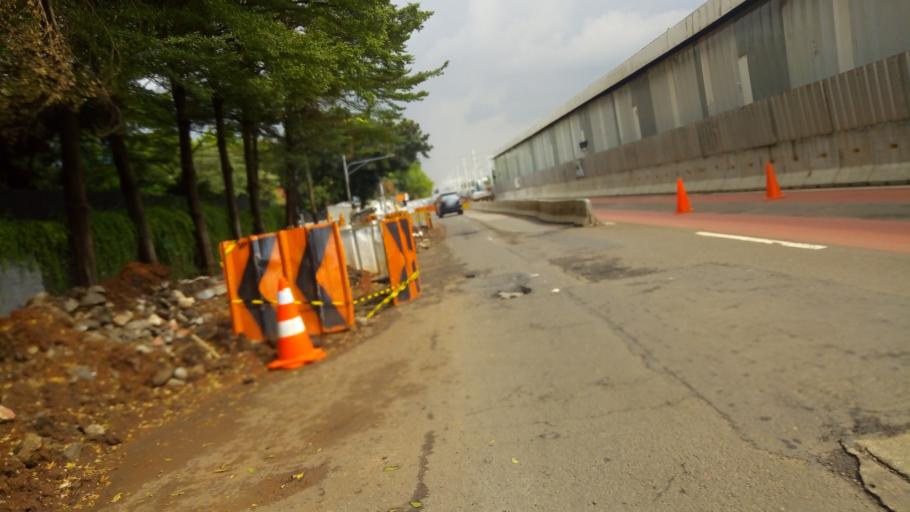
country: ID
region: Jakarta Raya
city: Jakarta
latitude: -6.2322
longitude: 106.7986
